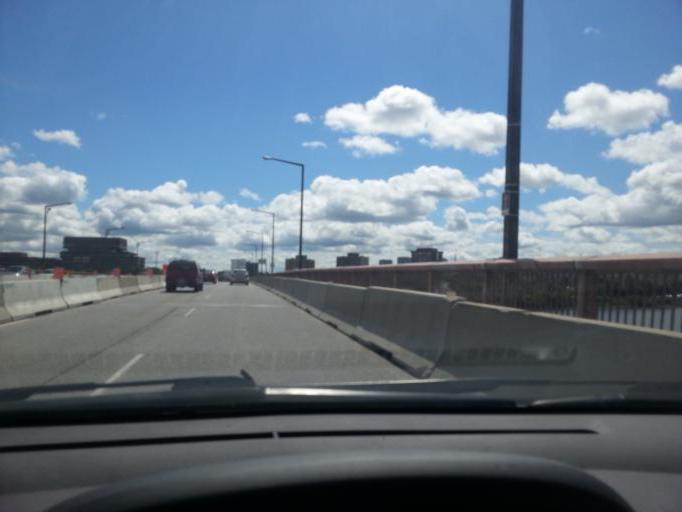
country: CA
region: Ontario
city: Ottawa
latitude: 45.4373
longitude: -75.7044
